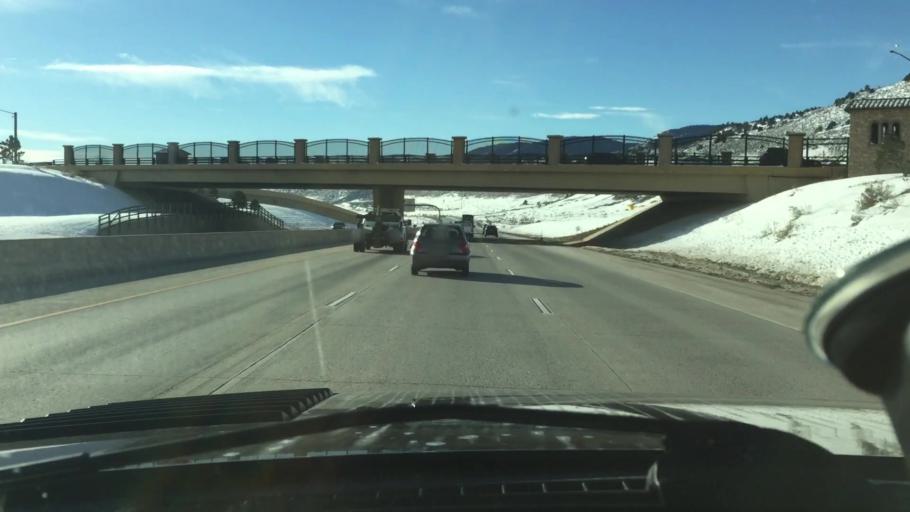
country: US
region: Colorado
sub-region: Jefferson County
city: West Pleasant View
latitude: 39.6878
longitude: -105.1884
